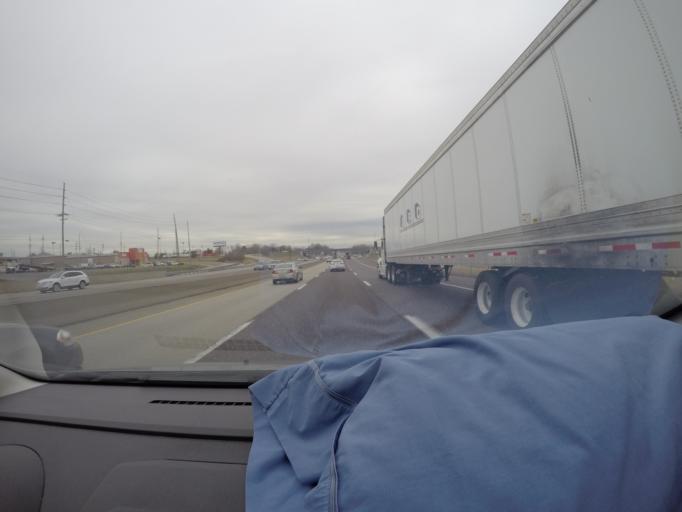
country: US
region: Missouri
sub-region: Saint Charles County
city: Saint Peters
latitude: 38.8021
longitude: -90.6550
